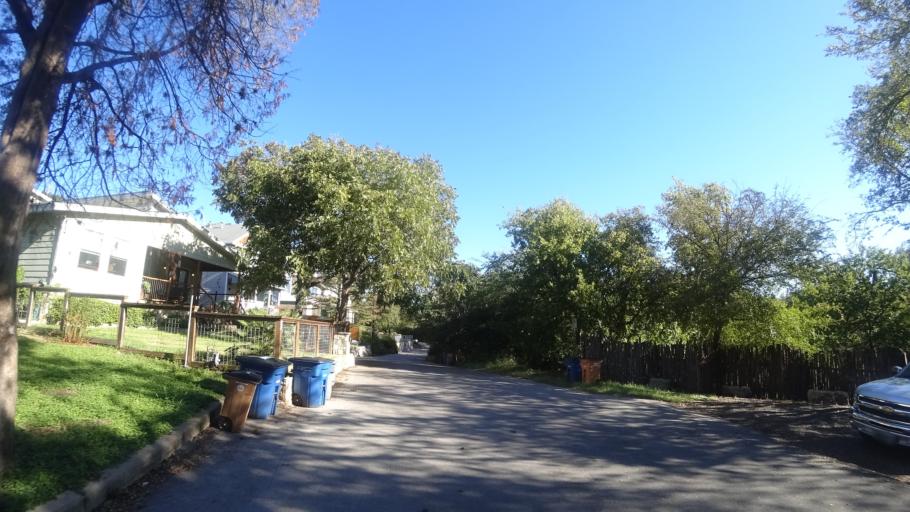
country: US
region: Texas
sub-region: Travis County
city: Rollingwood
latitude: 30.2805
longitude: -97.7702
